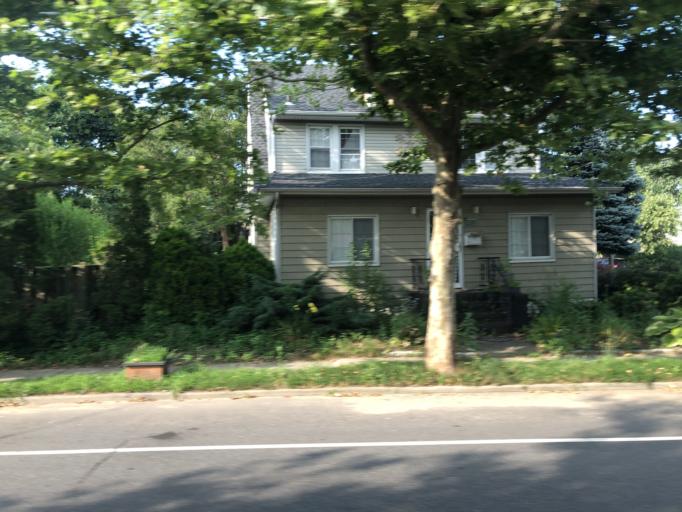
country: US
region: New York
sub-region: Nassau County
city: Malverne
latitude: 40.6730
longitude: -73.6752
